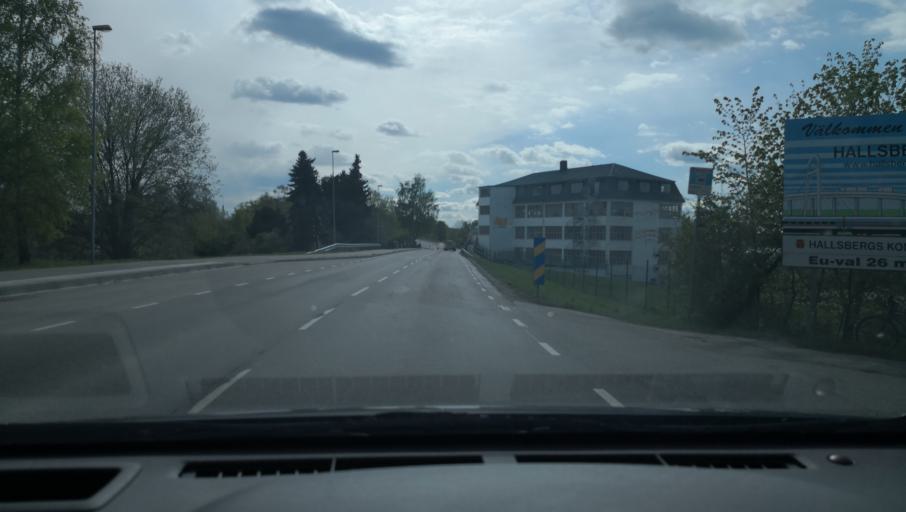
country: SE
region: OErebro
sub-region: Hallsbergs Kommun
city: Hallsberg
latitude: 59.0707
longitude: 15.1311
